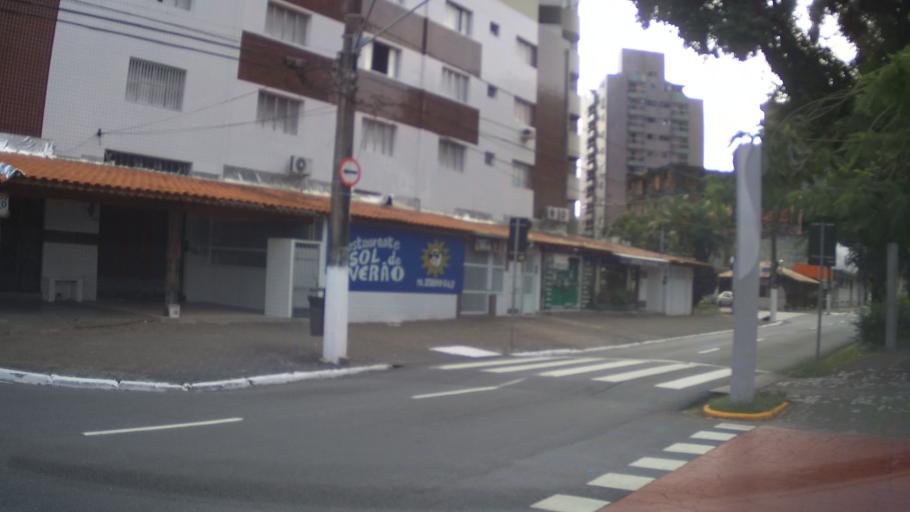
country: BR
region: Sao Paulo
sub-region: Praia Grande
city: Praia Grande
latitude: -24.0130
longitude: -46.4013
